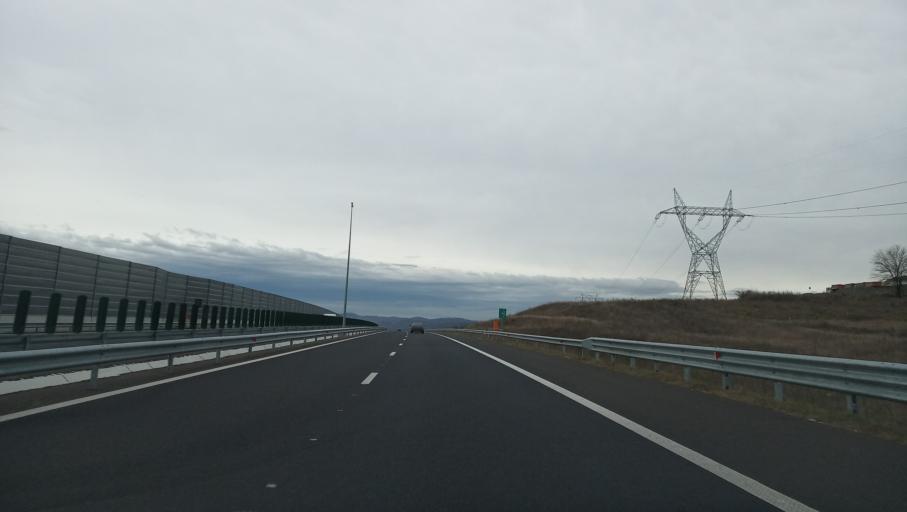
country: RO
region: Hunedoara
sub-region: Comuna Ilia
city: Ilia
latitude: 45.9465
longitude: 22.7192
